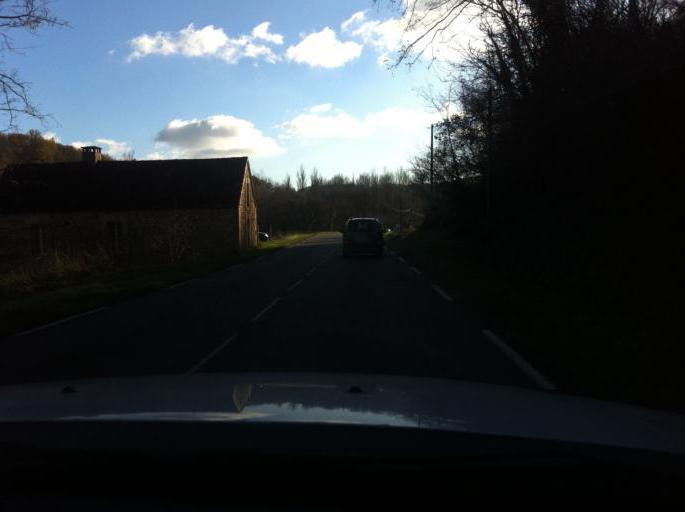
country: FR
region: Aquitaine
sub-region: Departement de la Dordogne
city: Rouffignac-Saint-Cernin-de-Reilhac
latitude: 45.0157
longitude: 0.9172
